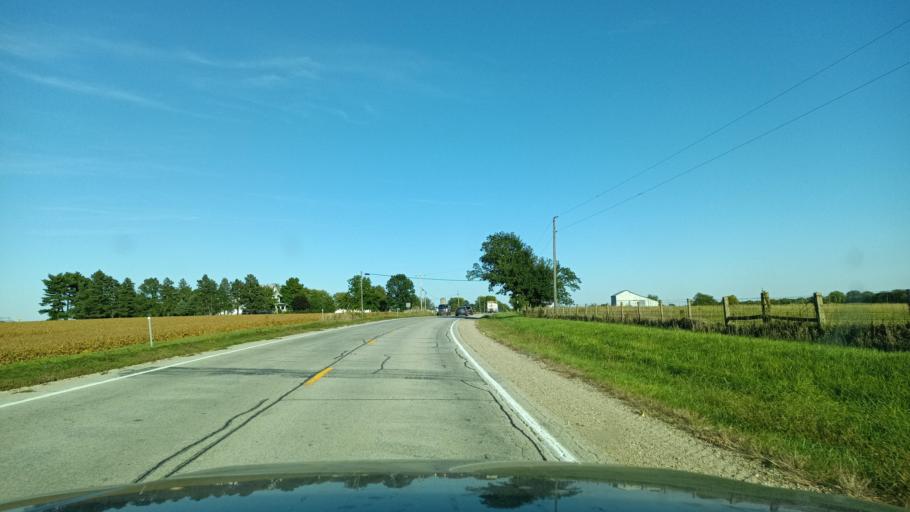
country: US
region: Illinois
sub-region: De Witt County
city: Farmer City
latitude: 40.2318
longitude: -88.6750
